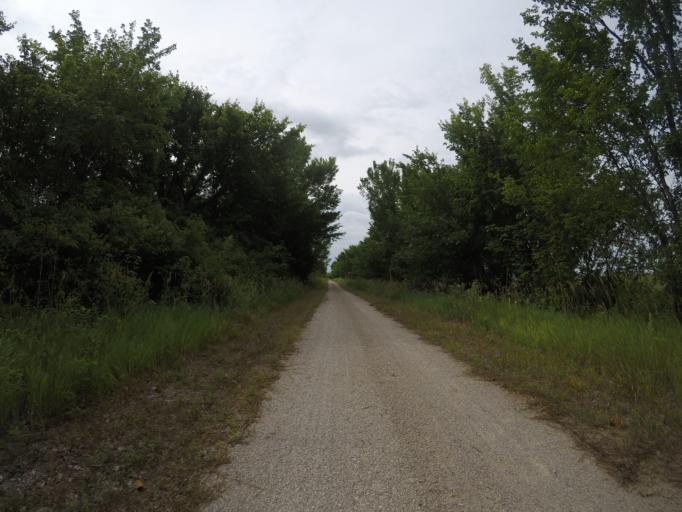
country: US
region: Kansas
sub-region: Franklin County
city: Ottawa
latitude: 38.5121
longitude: -95.2726
